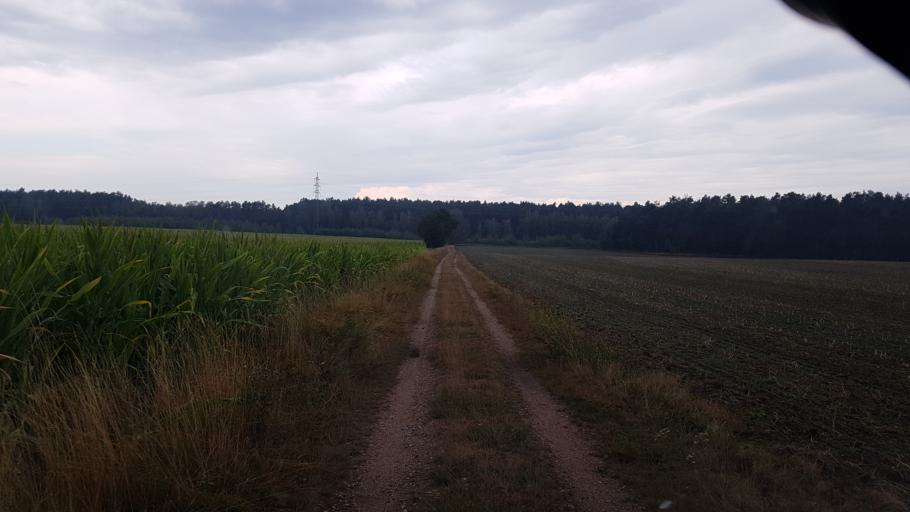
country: DE
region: Brandenburg
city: Finsterwalde
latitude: 51.6356
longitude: 13.7620
